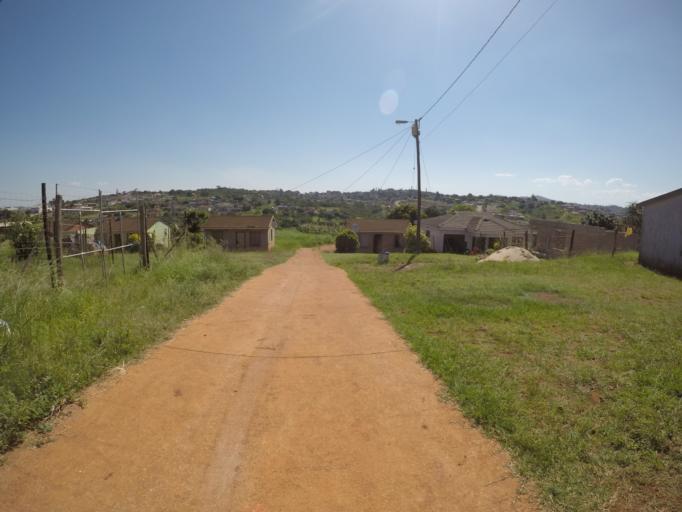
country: ZA
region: KwaZulu-Natal
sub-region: uThungulu District Municipality
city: Empangeni
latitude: -28.7723
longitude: 31.8762
